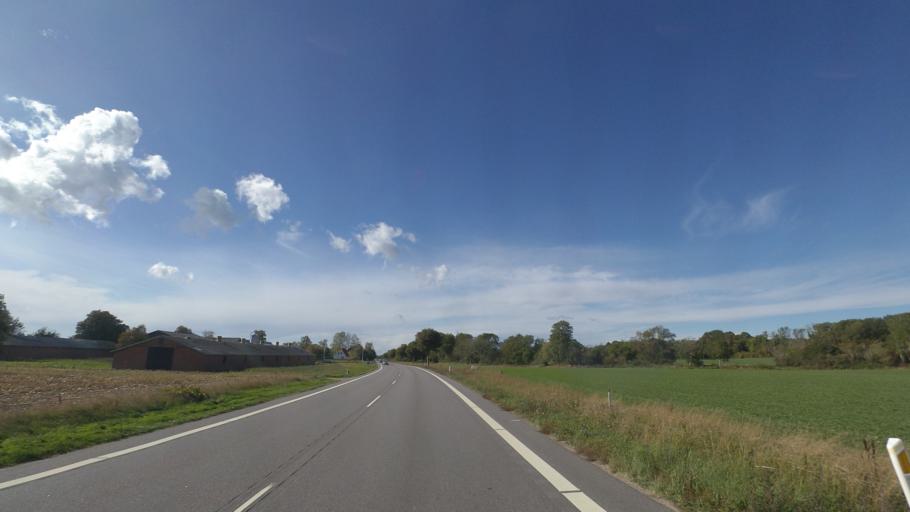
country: DK
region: Capital Region
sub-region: Bornholm Kommune
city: Ronne
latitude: 55.0742
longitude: 14.7943
